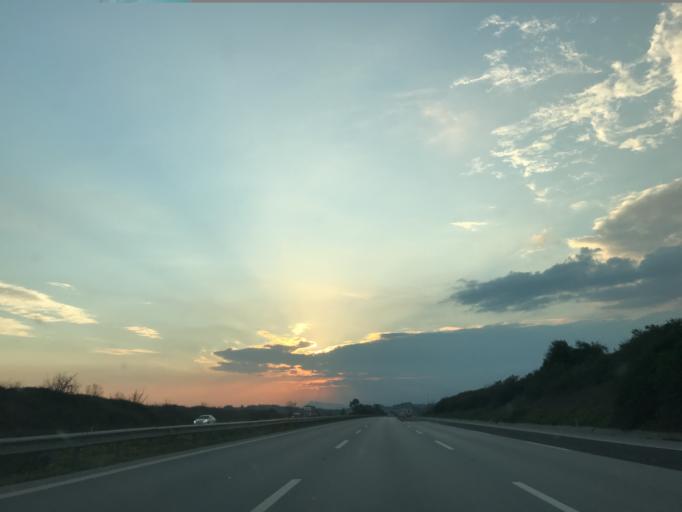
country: TR
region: Mersin
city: Yenice
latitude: 37.0215
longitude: 35.0386
